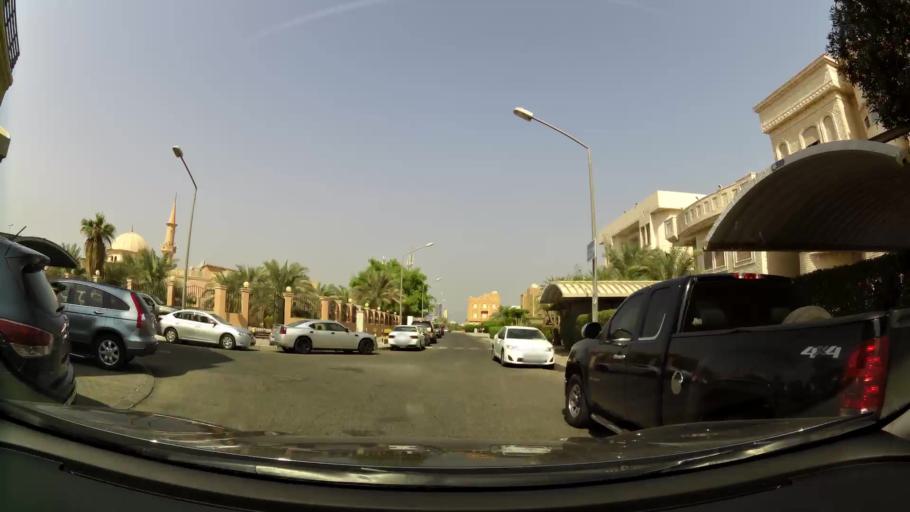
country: KW
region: Al Asimah
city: Ad Dasmah
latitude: 29.3529
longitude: 48.0114
